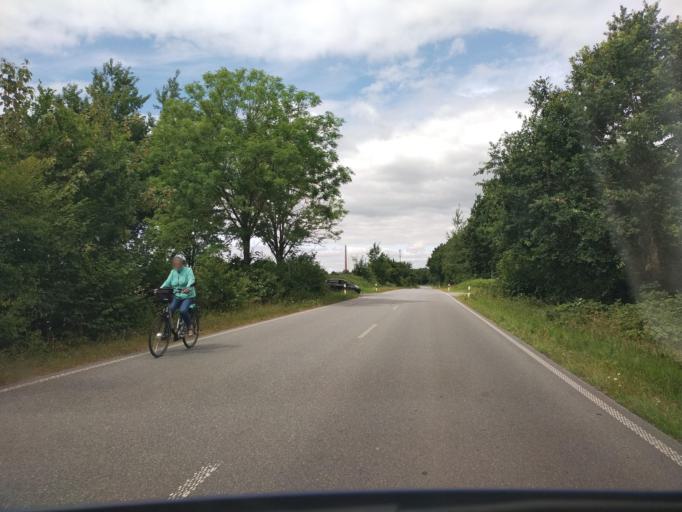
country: DE
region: Schleswig-Holstein
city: Schleswig
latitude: 54.5250
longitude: 9.5862
